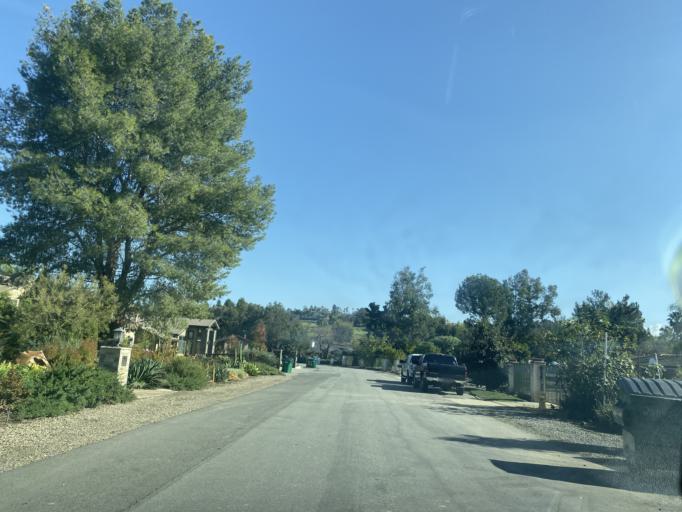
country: US
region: California
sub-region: Orange County
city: Villa Park
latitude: 33.8039
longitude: -117.7808
